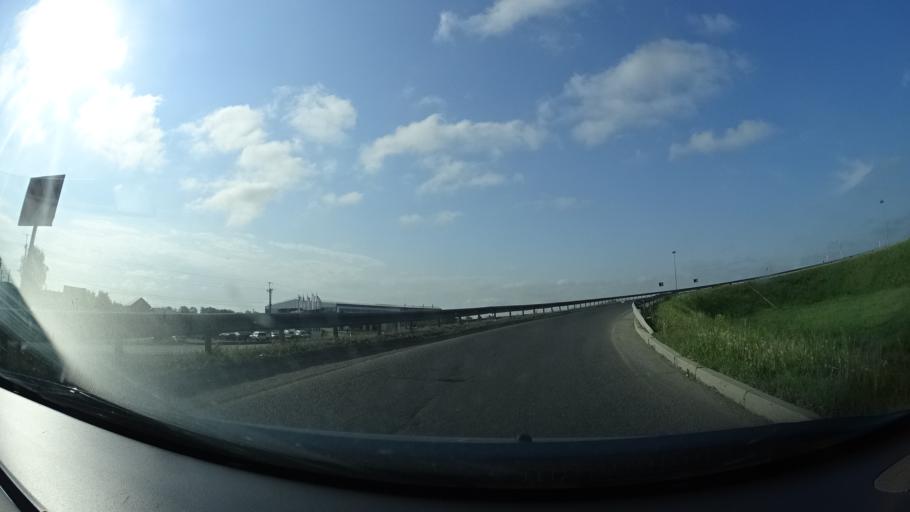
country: RU
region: Perm
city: Kondratovo
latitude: 57.9548
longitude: 56.1241
